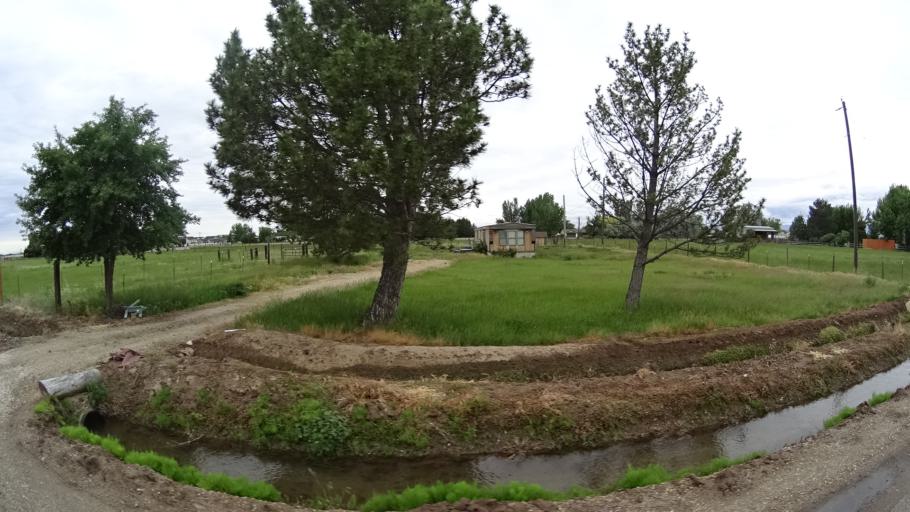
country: US
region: Idaho
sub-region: Ada County
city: Star
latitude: 43.6486
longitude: -116.4513
